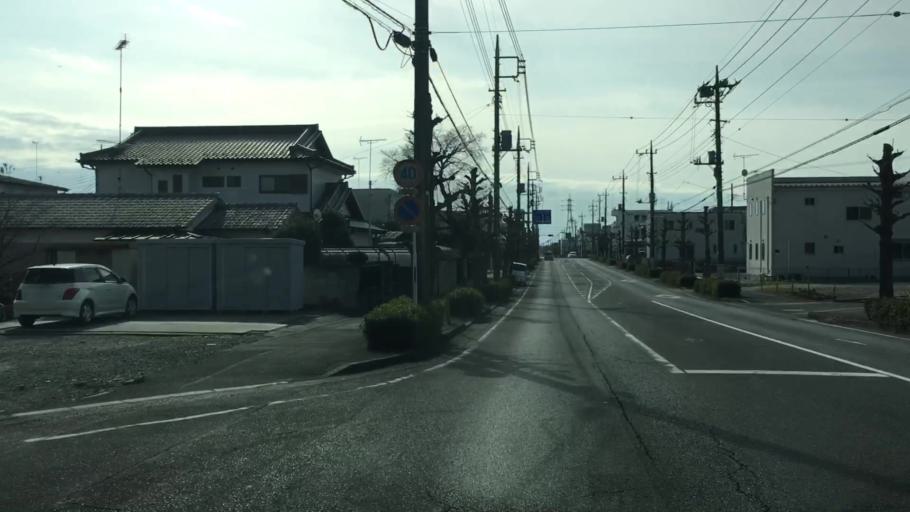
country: JP
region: Saitama
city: Menuma
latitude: 36.2427
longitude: 139.4086
